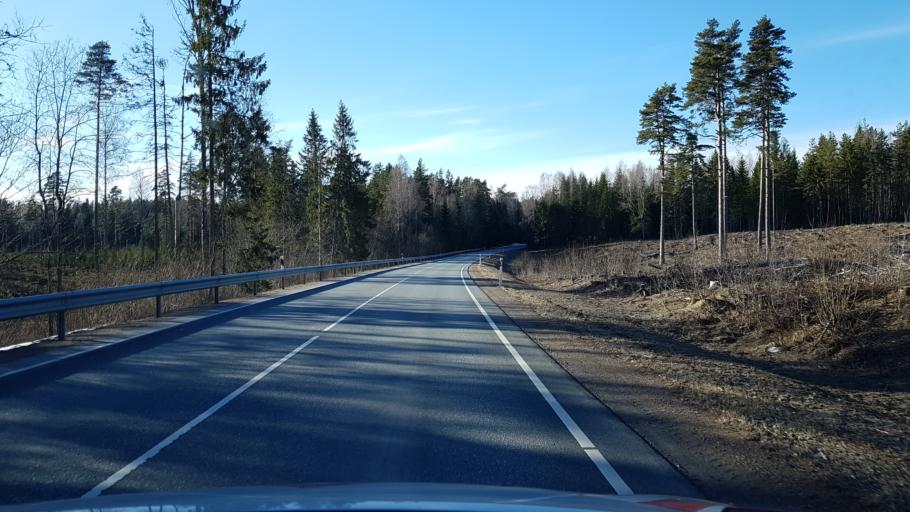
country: EE
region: Laeaene-Virumaa
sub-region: Tapa vald
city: Tapa
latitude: 59.4023
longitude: 26.0088
